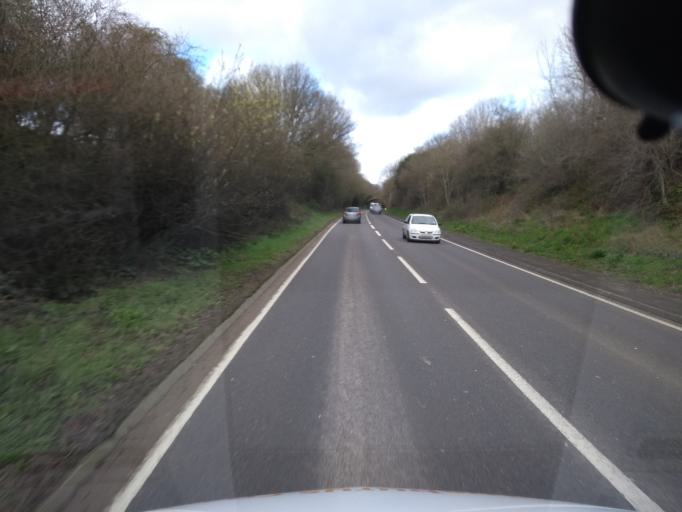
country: GB
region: England
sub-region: Somerset
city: Yeovil
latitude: 50.9413
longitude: -2.6796
